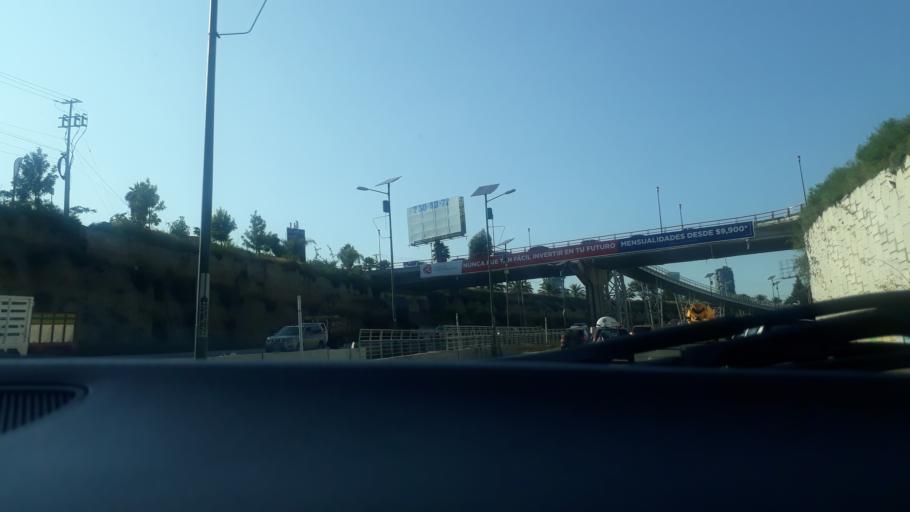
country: MX
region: Puebla
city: Tlazcalancingo
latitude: 18.9995
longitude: -98.2599
